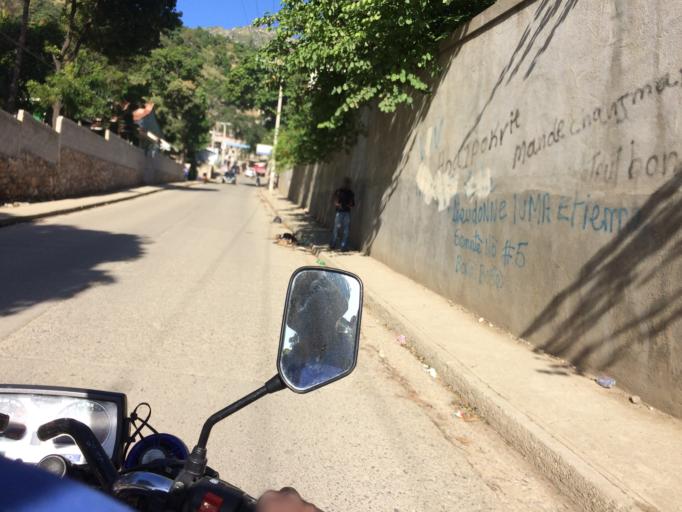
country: HT
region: Nord
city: Okap
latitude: 19.7547
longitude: -72.2111
